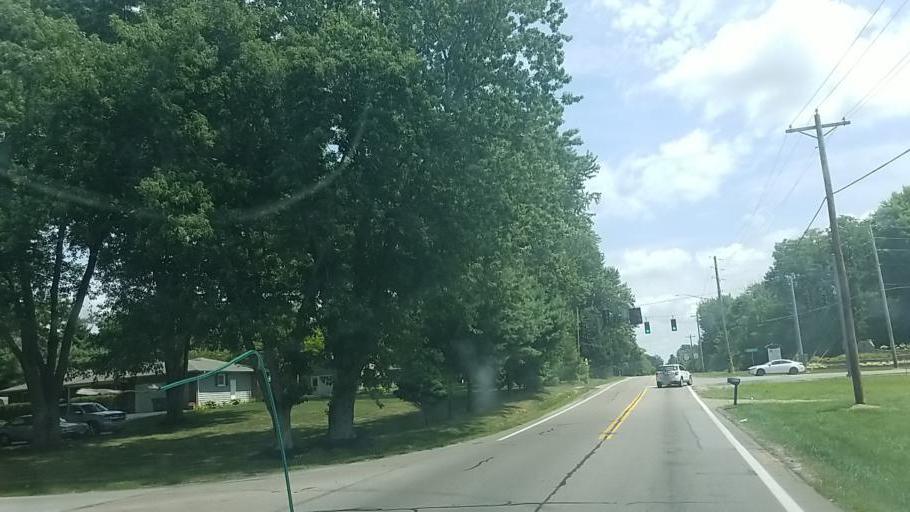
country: US
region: Ohio
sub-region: Fairfield County
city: Pickerington
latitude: 39.9304
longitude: -82.7462
